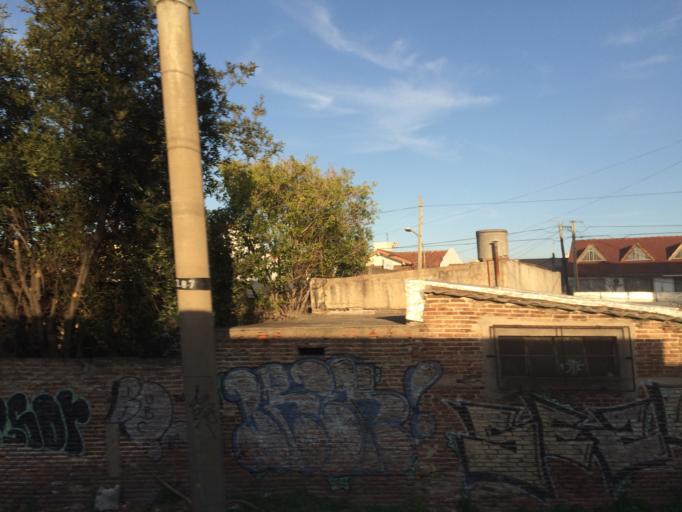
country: AR
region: Buenos Aires
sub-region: Partido de Lanus
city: Lanus
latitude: -34.7000
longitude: -58.3879
